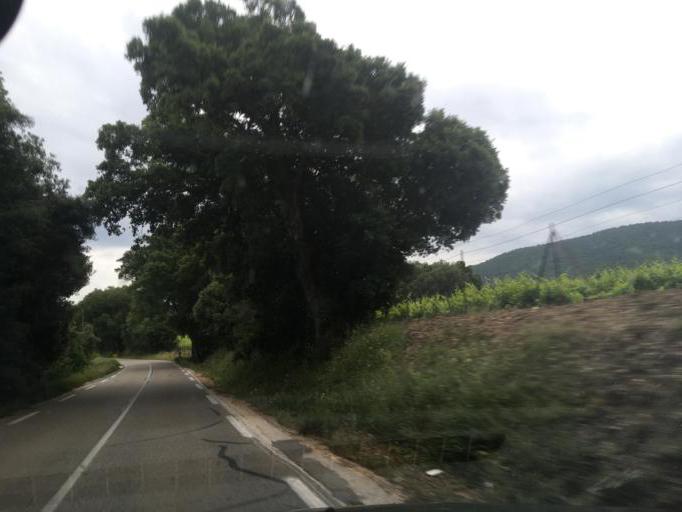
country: FR
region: Provence-Alpes-Cote d'Azur
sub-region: Departement du Var
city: Pierrefeu-du-Var
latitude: 43.2329
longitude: 6.1975
